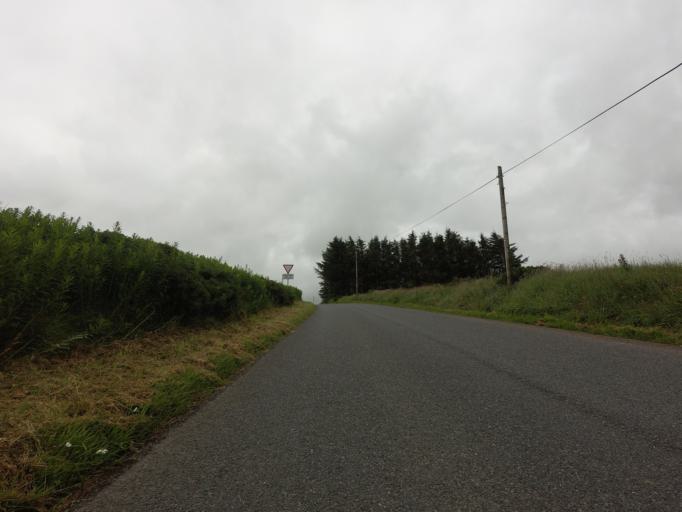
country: GB
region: Scotland
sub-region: Aberdeenshire
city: Rosehearty
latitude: 57.5436
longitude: -2.2468
